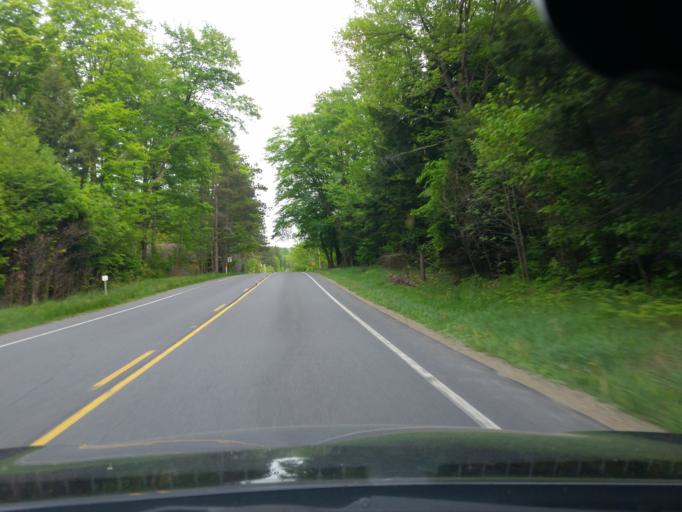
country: US
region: Pennsylvania
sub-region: McKean County
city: Kane
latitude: 41.5740
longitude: -78.9158
